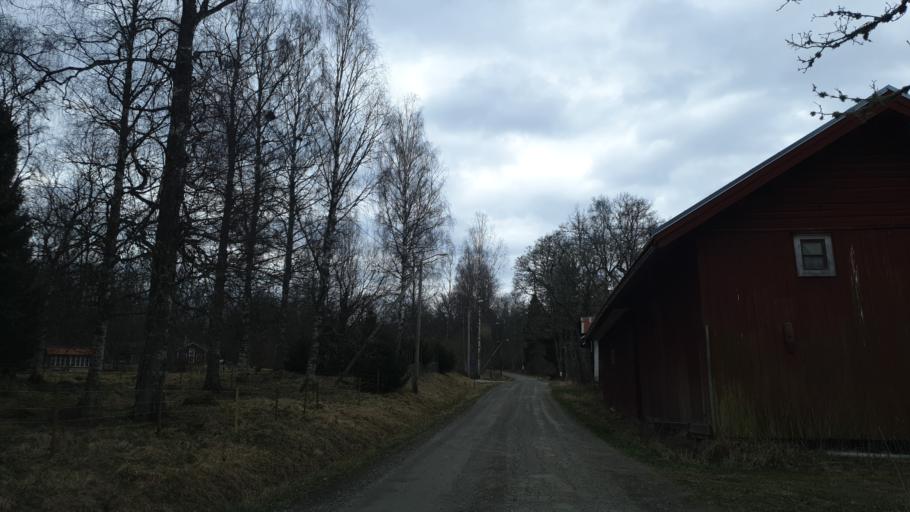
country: SE
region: OErebro
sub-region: Nora Kommun
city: As
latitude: 59.5998
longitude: 14.9047
